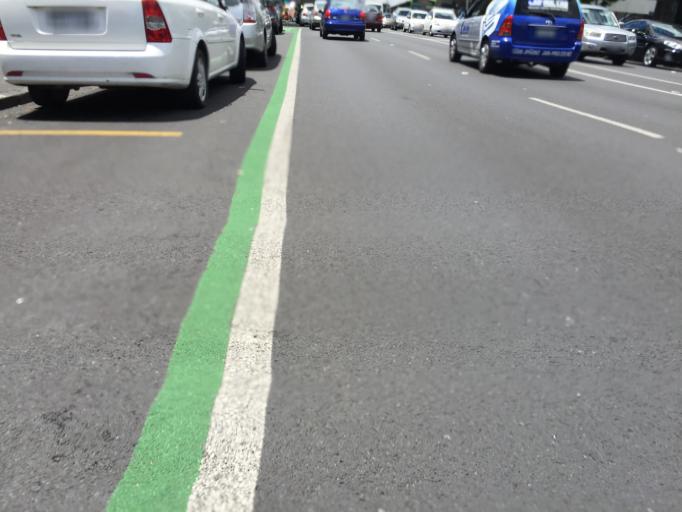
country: NZ
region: Auckland
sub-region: Auckland
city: Auckland
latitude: -36.8589
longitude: 174.7514
